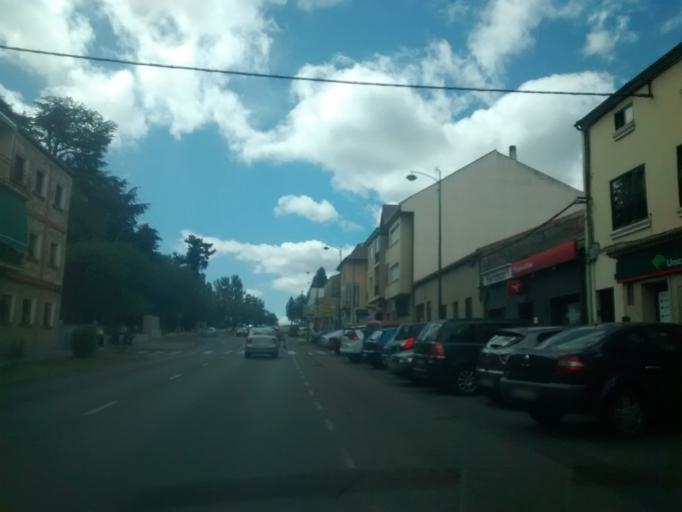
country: ES
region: Castille and Leon
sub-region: Provincia de Salamanca
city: Ciudad Rodrigo
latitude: 40.6015
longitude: -6.5314
